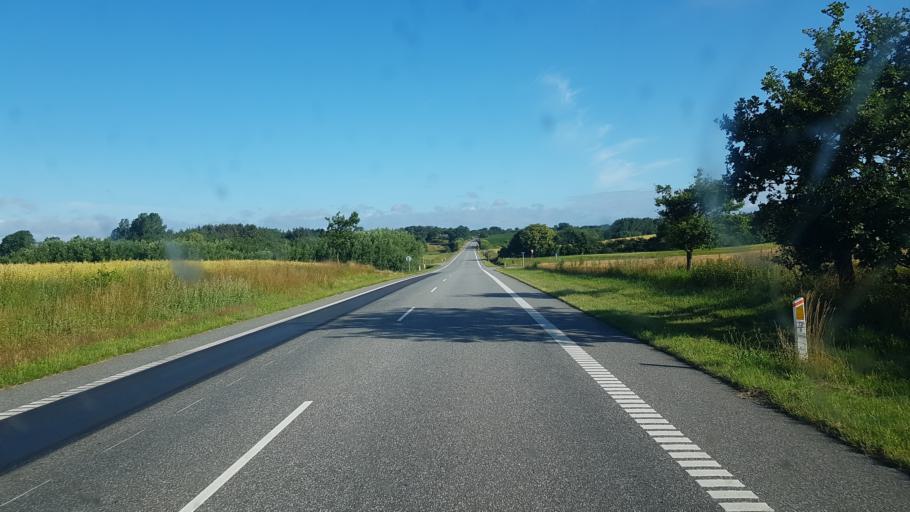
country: DK
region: South Denmark
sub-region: Vejen Kommune
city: Rodding
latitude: 55.3856
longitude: 9.0484
